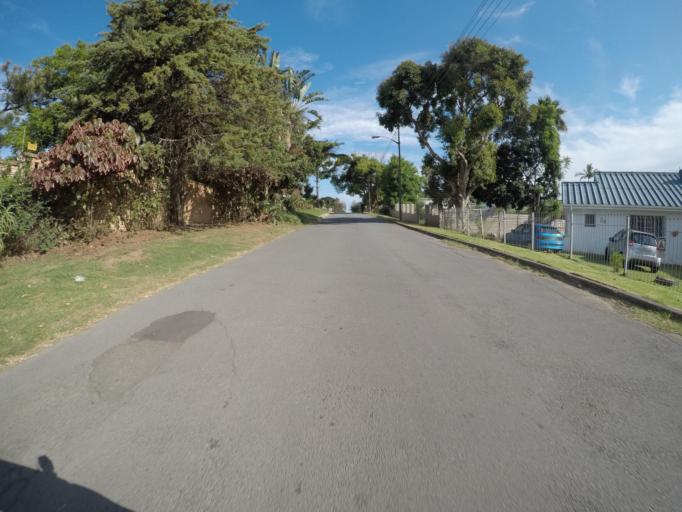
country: ZA
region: Eastern Cape
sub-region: Buffalo City Metropolitan Municipality
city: East London
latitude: -32.9413
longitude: 28.0048
